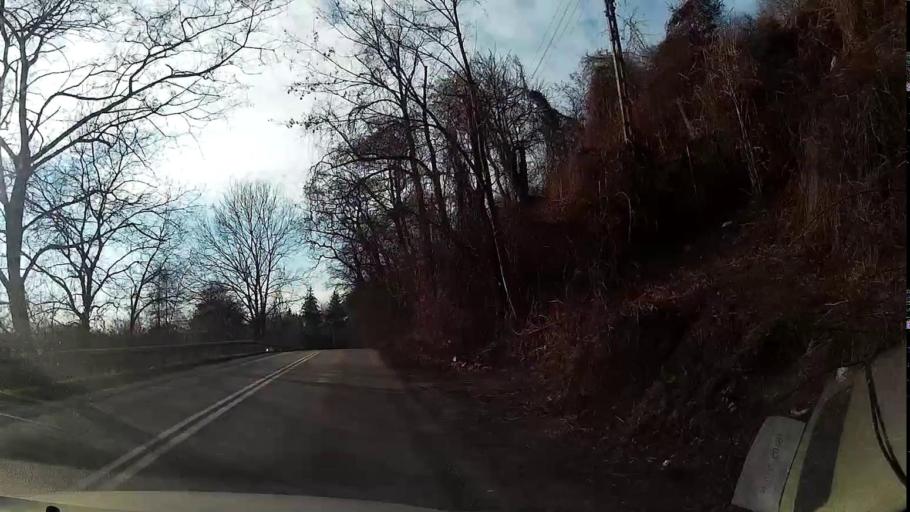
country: PL
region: Lesser Poland Voivodeship
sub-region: Powiat krakowski
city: Rzaska
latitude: 50.0464
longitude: 19.8629
